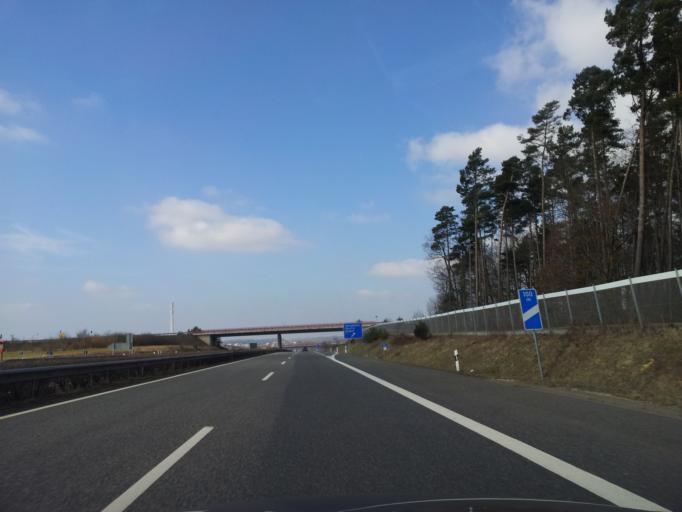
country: DE
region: Rheinland-Pfalz
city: Gransdorf
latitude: 50.0072
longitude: 6.6936
